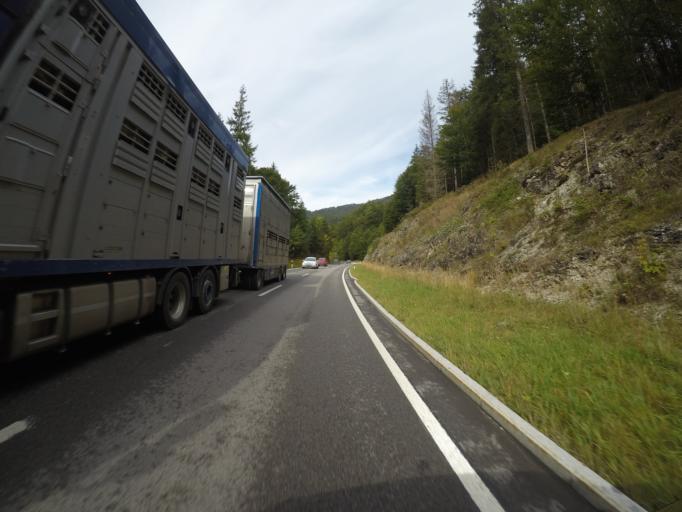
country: DE
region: Bavaria
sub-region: Upper Bavaria
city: Lenggries
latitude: 47.5821
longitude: 11.6093
